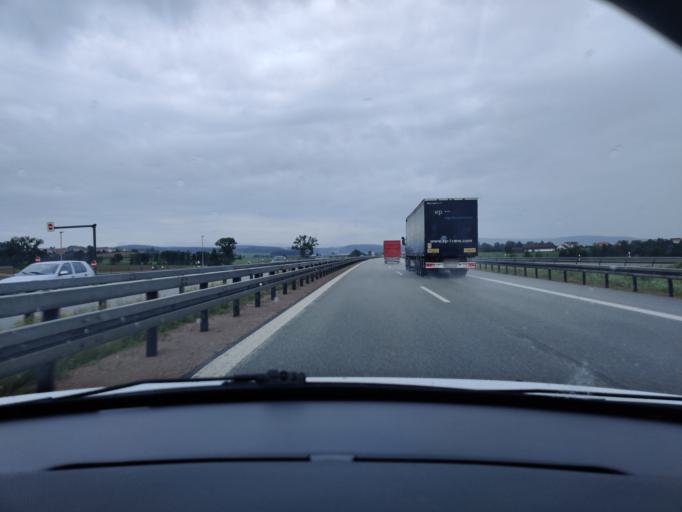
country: DE
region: Bavaria
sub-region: Upper Palatinate
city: Pfreimd
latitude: 49.4744
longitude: 12.1926
